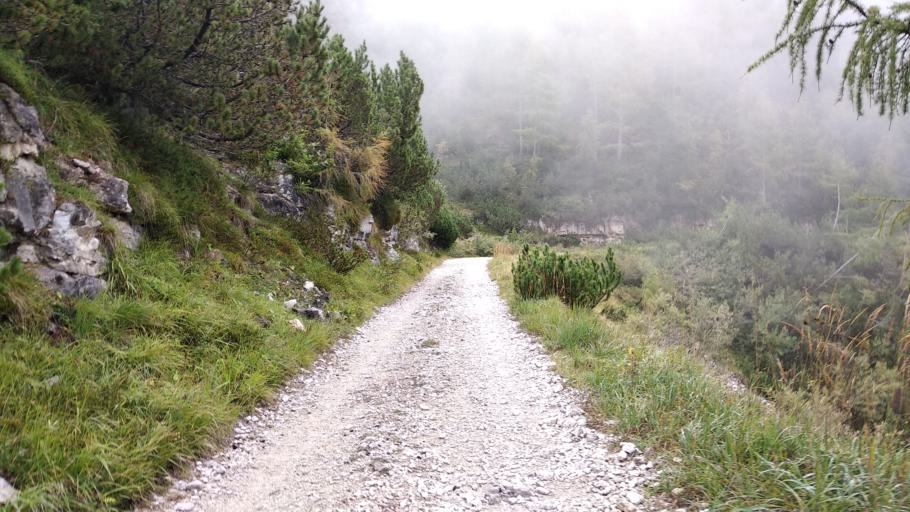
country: IT
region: Trentino-Alto Adige
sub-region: Provincia di Trento
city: Borgo
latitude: 45.9660
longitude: 11.4388
